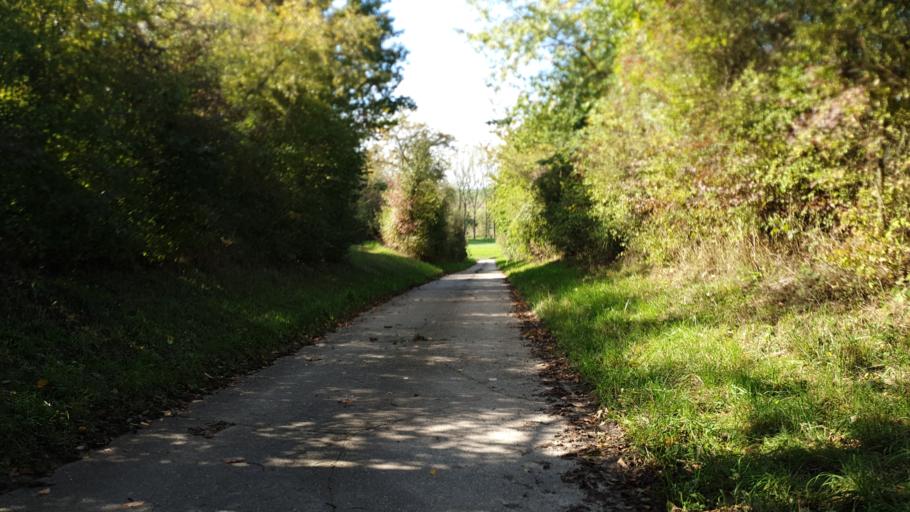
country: DE
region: Rheinland-Pfalz
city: Oberhausen
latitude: 49.1180
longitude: 8.0598
